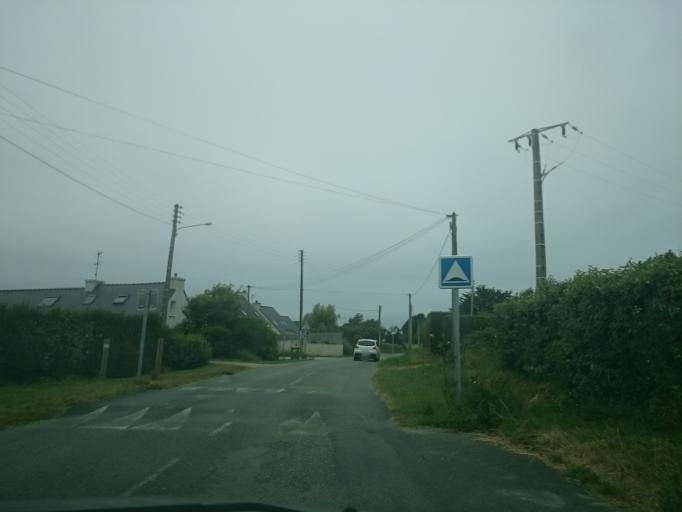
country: FR
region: Brittany
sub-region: Departement du Finistere
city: Saint-Pabu
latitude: 48.5689
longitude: -4.6241
